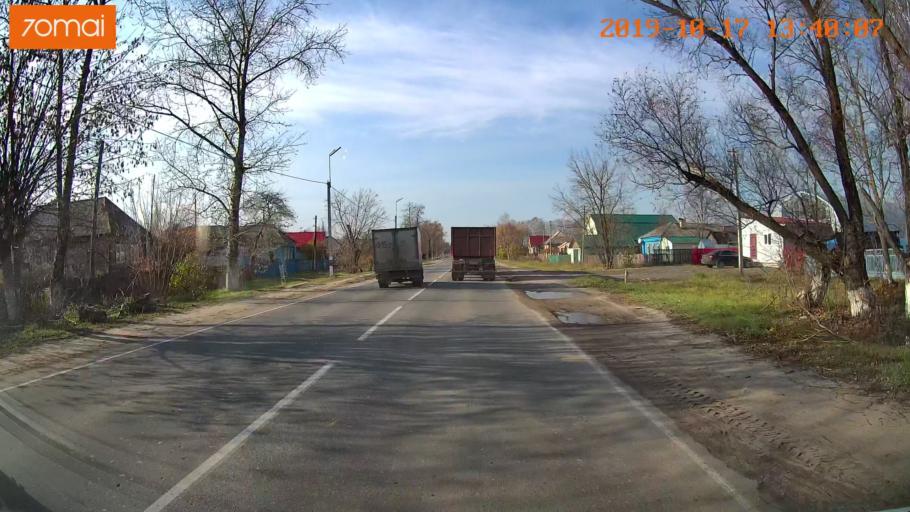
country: RU
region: Rjazan
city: Tuma
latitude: 55.1471
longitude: 40.5771
